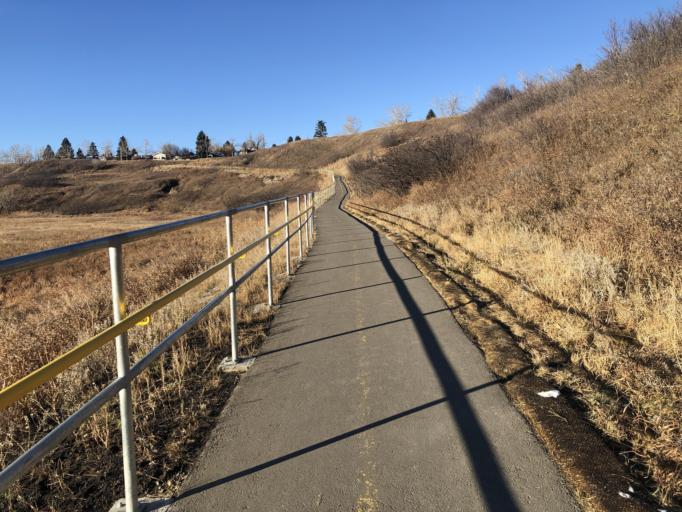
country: CA
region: Alberta
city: Calgary
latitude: 50.9112
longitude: -114.0230
